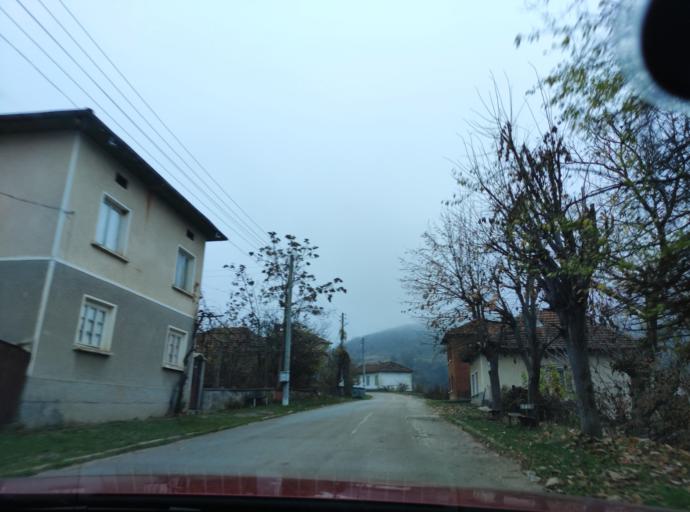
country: BG
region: Lovech
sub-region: Obshtina Yablanitsa
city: Yablanitsa
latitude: 43.1174
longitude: 24.0638
